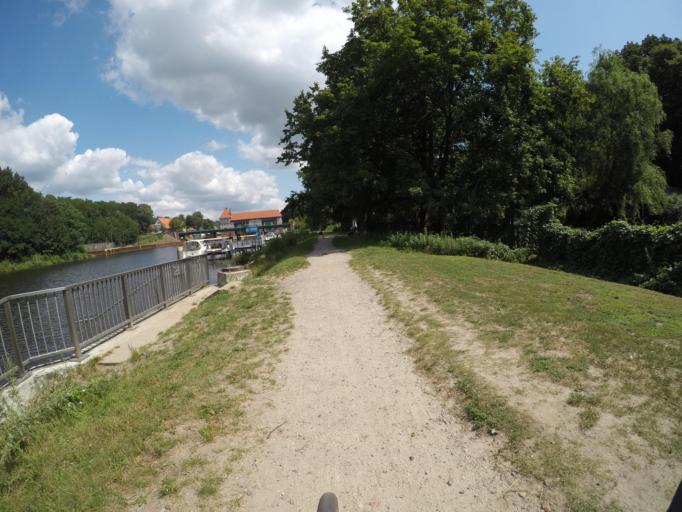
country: DE
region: Brandenburg
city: Stahnsdorf
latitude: 52.3949
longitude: 13.2051
